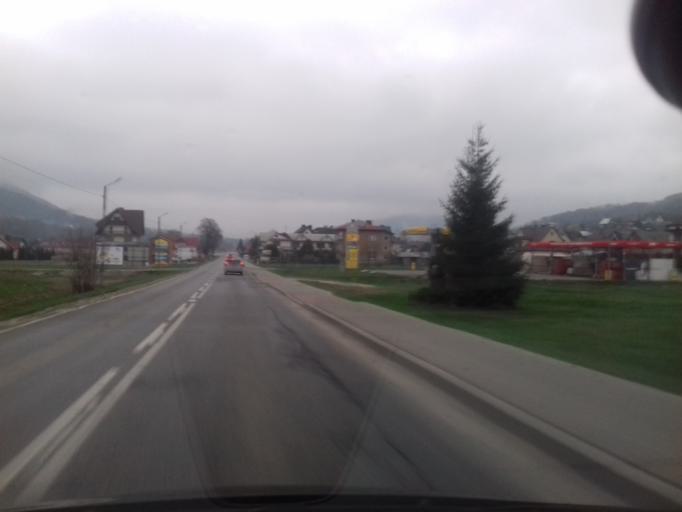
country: PL
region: Lesser Poland Voivodeship
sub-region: Powiat limanowski
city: Mszana Dolna
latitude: 49.6815
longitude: 20.0564
